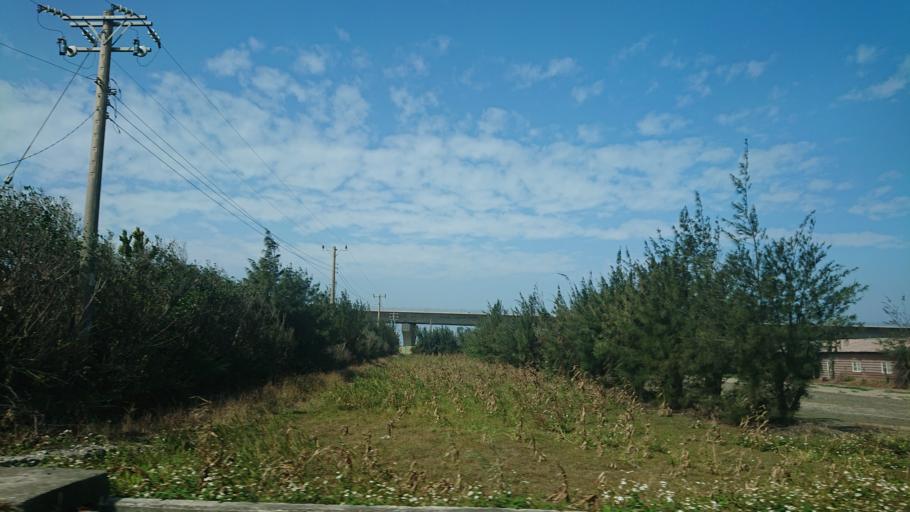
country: TW
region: Taiwan
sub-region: Changhua
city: Chang-hua
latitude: 23.9156
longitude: 120.3120
